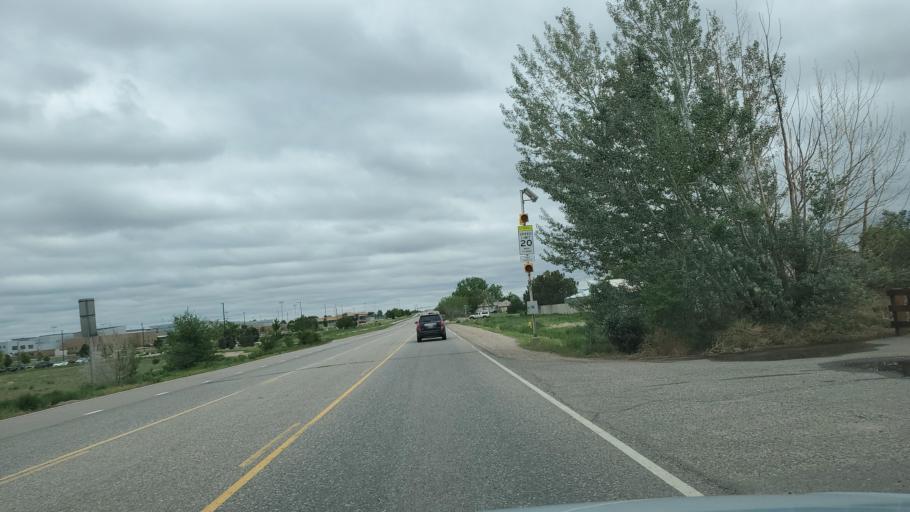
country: US
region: Colorado
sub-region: Adams County
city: Todd Creek
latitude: 39.9144
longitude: -104.8452
